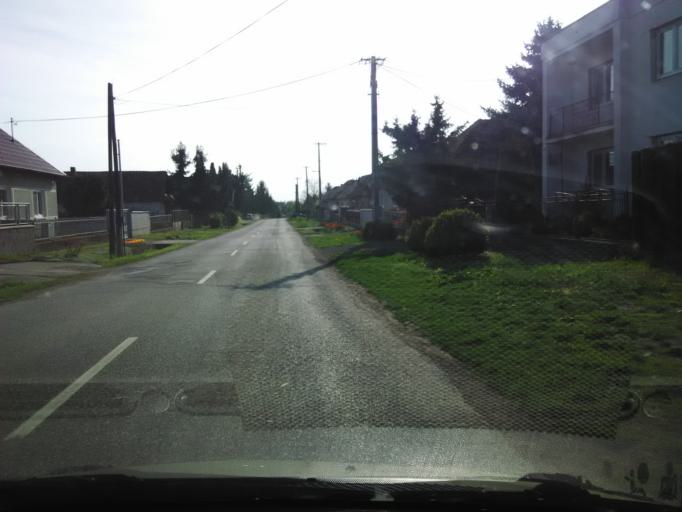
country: SK
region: Nitriansky
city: Levice
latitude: 48.2805
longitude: 18.6445
